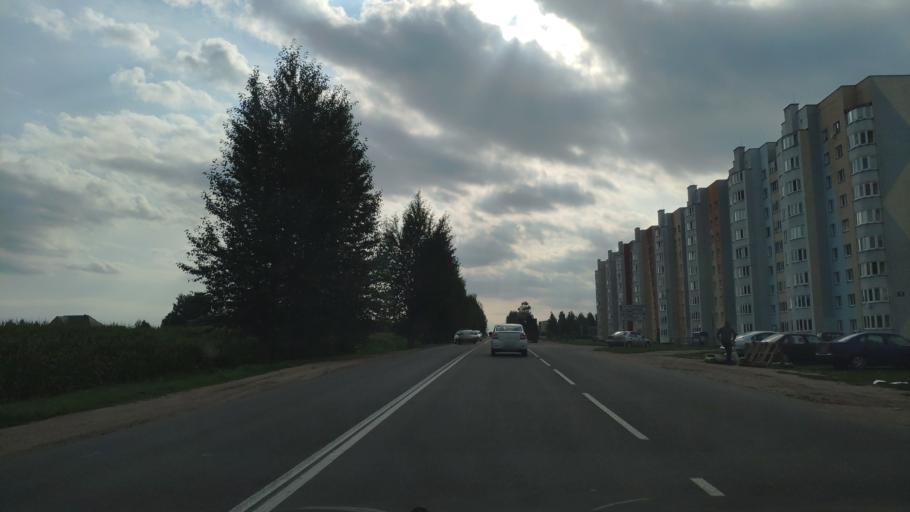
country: BY
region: Minsk
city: Azyartso
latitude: 53.8421
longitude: 27.4047
